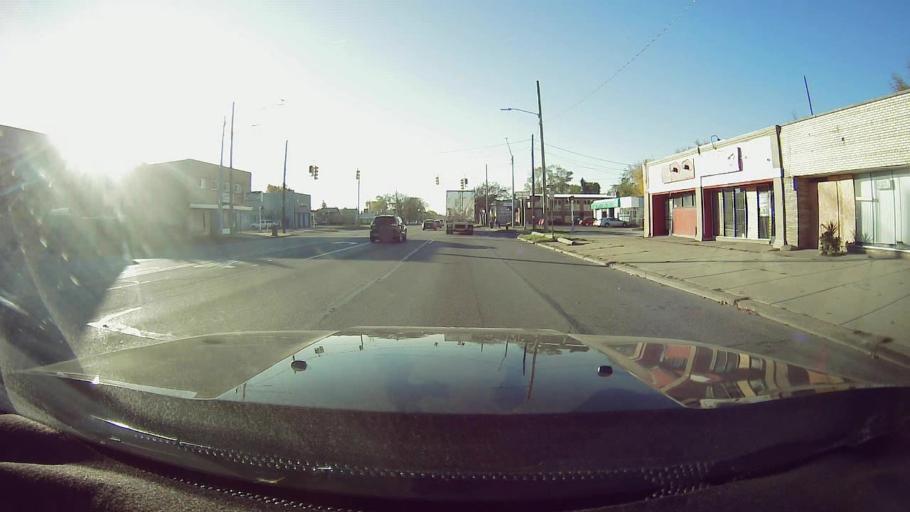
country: US
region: Michigan
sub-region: Macomb County
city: Warren
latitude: 42.4395
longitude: -83.0246
